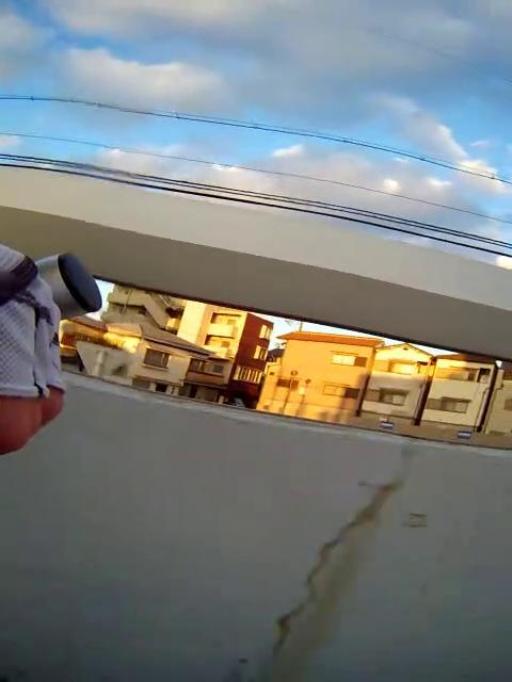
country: JP
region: Osaka
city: Osaka-shi
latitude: 34.7233
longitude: 135.4727
